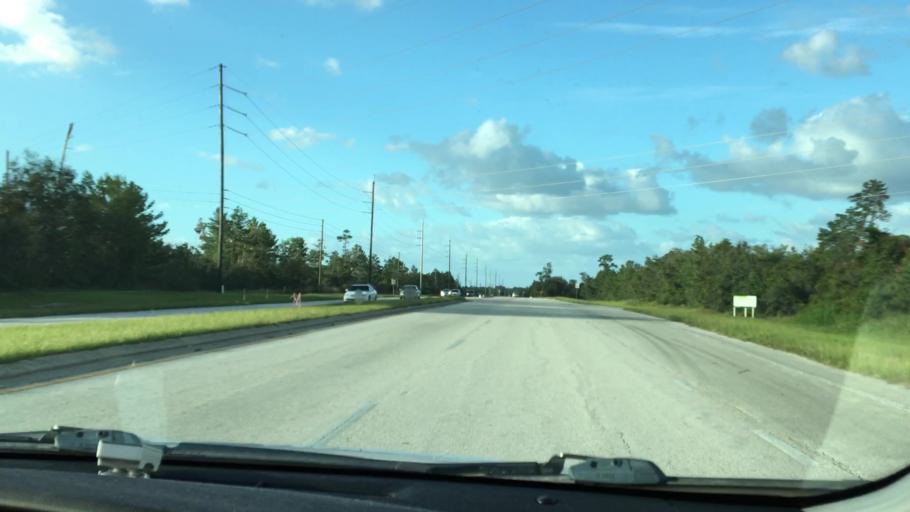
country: US
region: Florida
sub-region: Volusia County
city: Deltona
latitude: 28.9195
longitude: -81.2817
